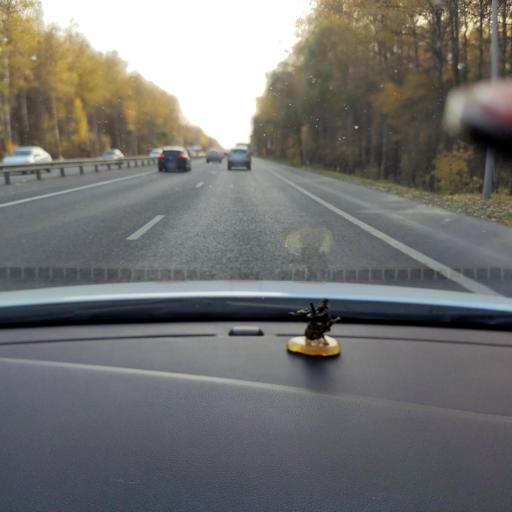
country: RU
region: Tatarstan
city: Osinovo
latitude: 55.8423
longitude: 48.8516
